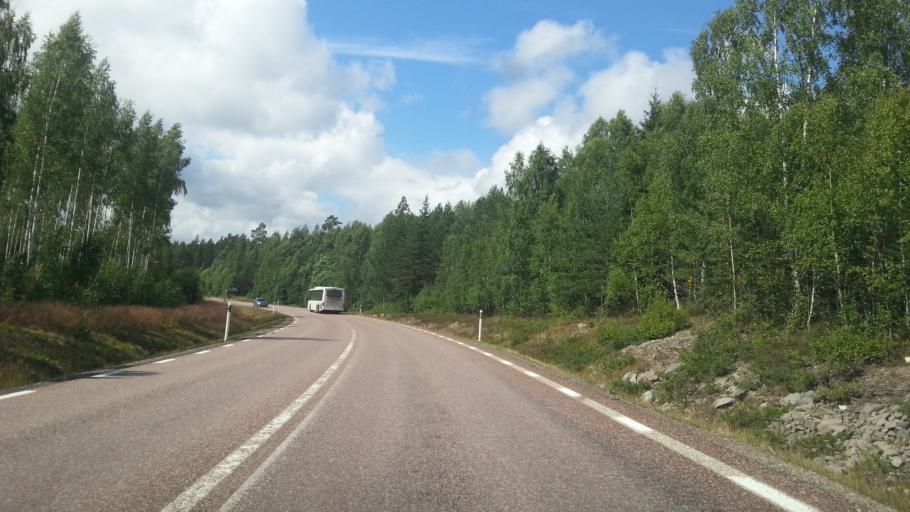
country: SE
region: Dalarna
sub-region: Faluns Kommun
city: Falun
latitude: 60.6135
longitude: 15.7283
